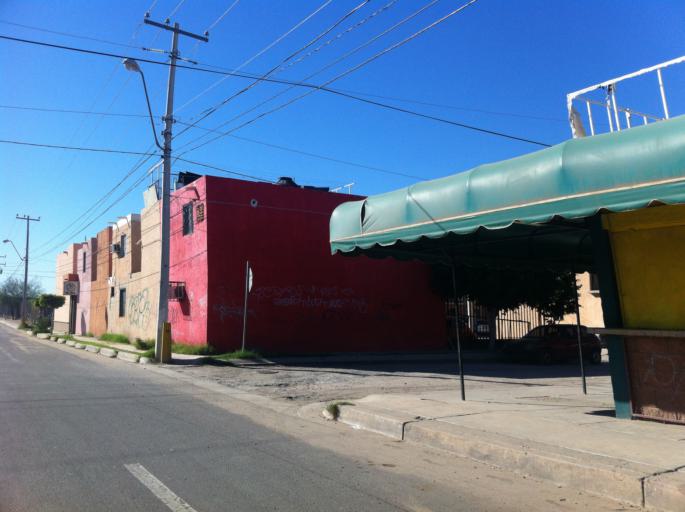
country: MX
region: Sonora
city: Hermosillo
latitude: 29.1184
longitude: -110.9995
